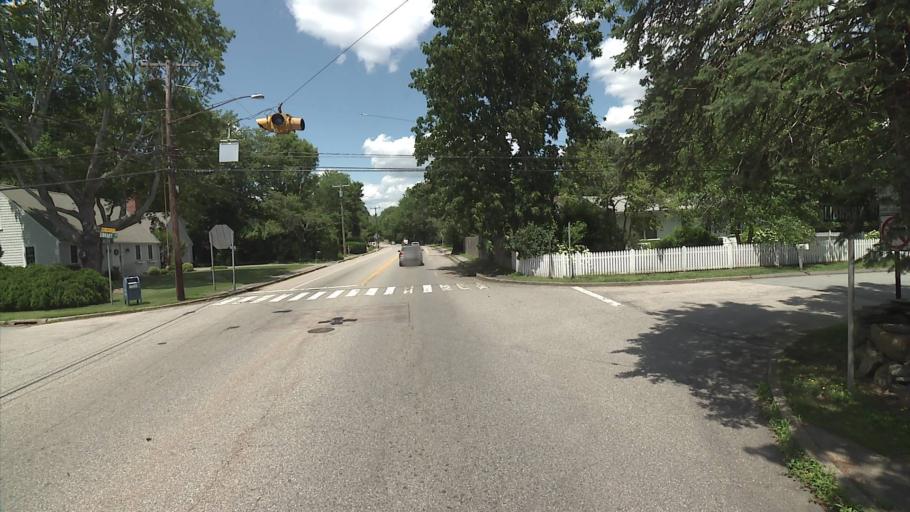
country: US
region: Connecticut
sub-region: New London County
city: Mystic
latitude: 41.3541
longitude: -71.9779
